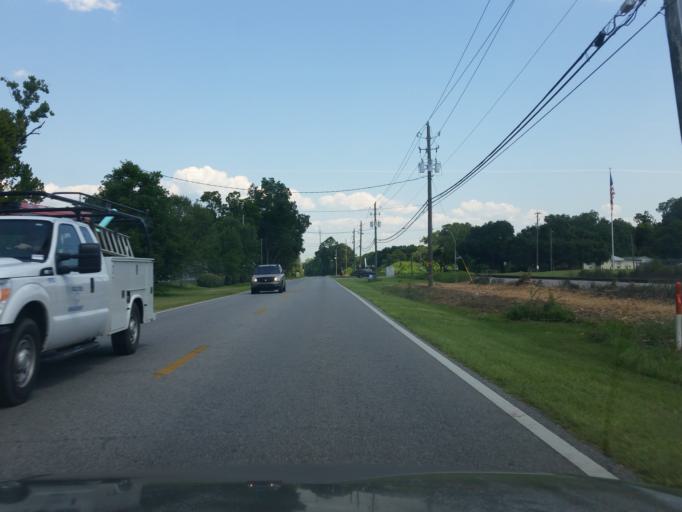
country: US
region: Florida
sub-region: Escambia County
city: Gonzalez
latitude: 30.6003
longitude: -87.3126
